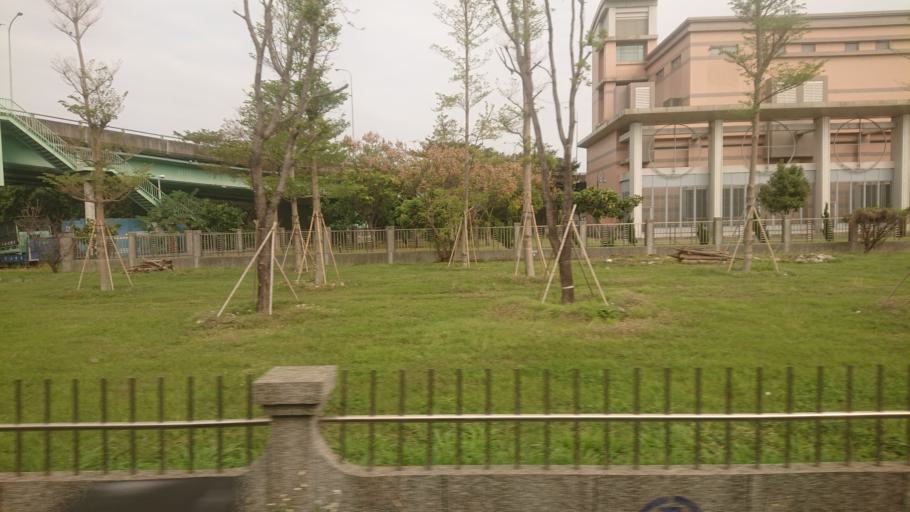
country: TW
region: Taiwan
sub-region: Changhua
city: Chang-hua
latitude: 24.1107
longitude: 120.6065
